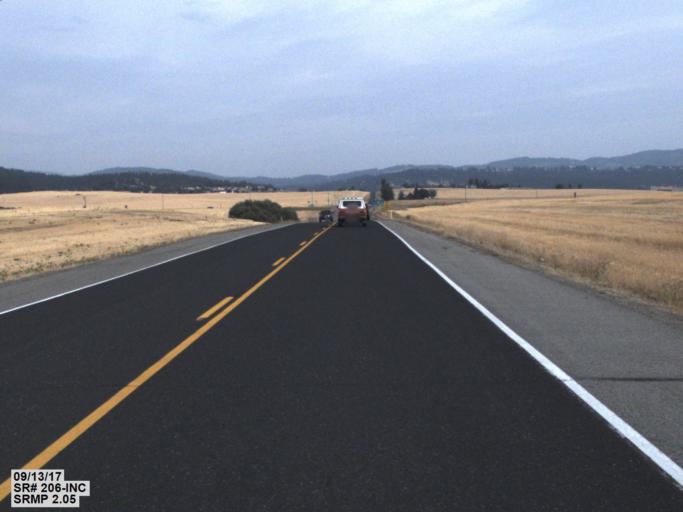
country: US
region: Washington
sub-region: Spokane County
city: Mead
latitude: 47.7875
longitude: -117.3110
